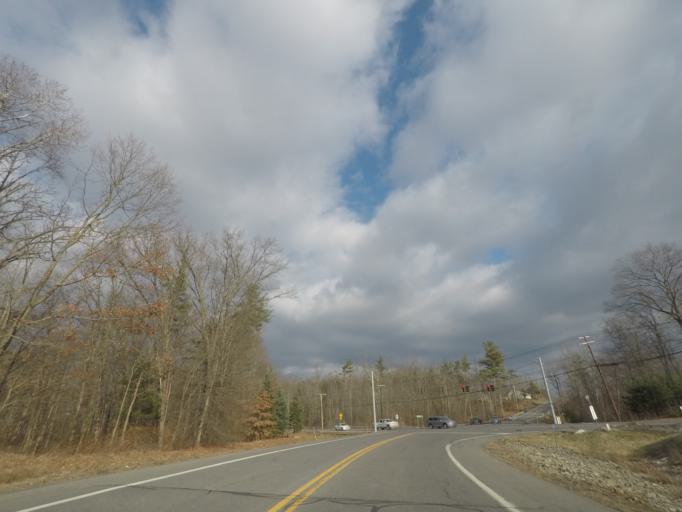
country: US
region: New York
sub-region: Albany County
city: Voorheesville
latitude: 42.6582
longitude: -73.9166
